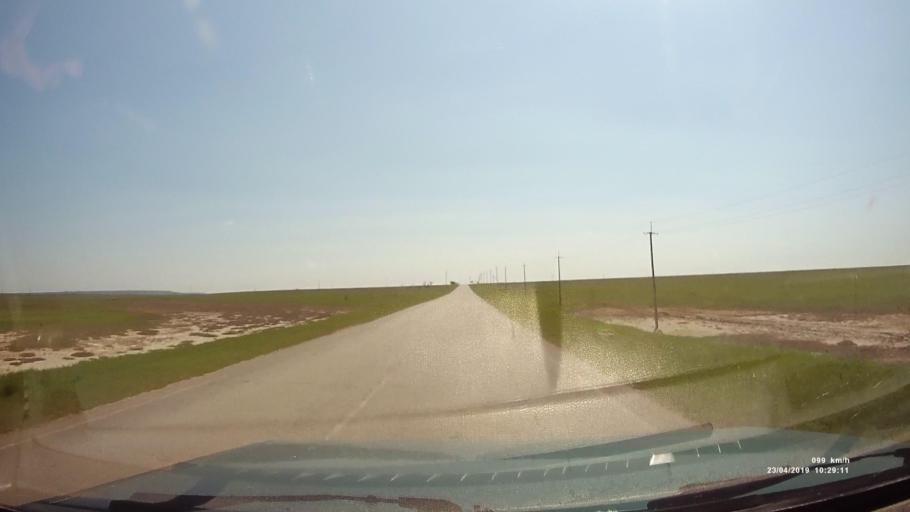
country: RU
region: Kalmykiya
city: Yashalta
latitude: 46.6001
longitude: 42.5219
